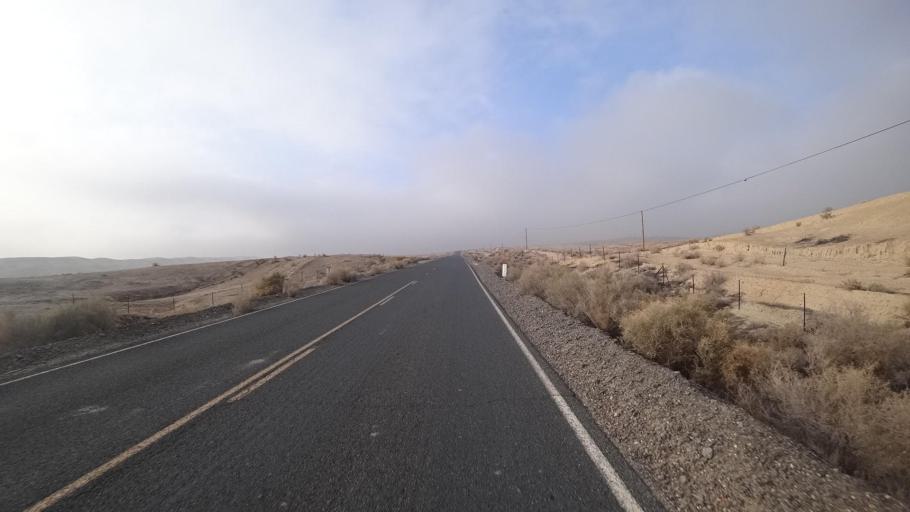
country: US
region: California
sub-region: Kern County
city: Ford City
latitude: 35.2430
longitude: -119.4551
